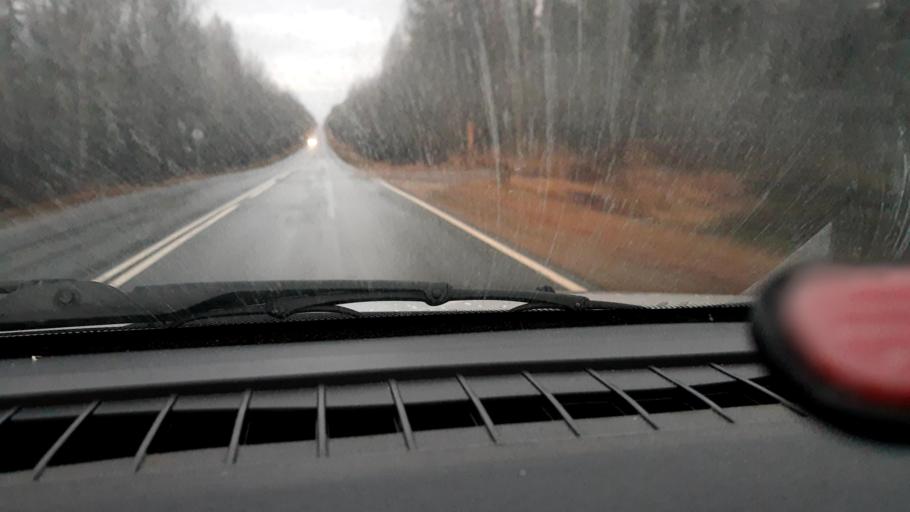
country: RU
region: Nizjnij Novgorod
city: Uren'
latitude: 57.2652
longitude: 45.6201
